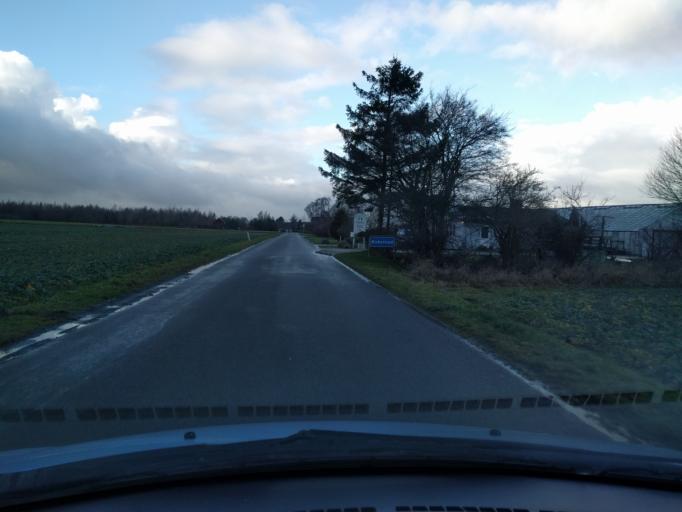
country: DK
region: South Denmark
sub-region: Kerteminde Kommune
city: Langeskov
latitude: 55.3918
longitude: 10.5676
